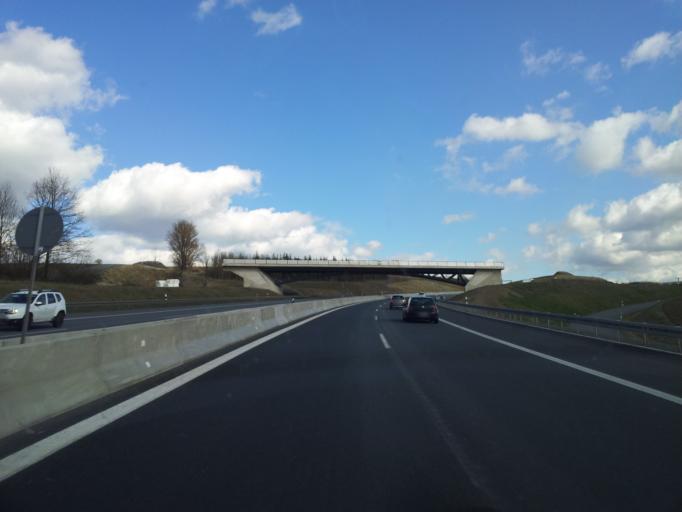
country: DE
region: Bavaria
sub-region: Upper Franconia
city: Harsdorf
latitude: 50.0286
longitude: 11.5872
